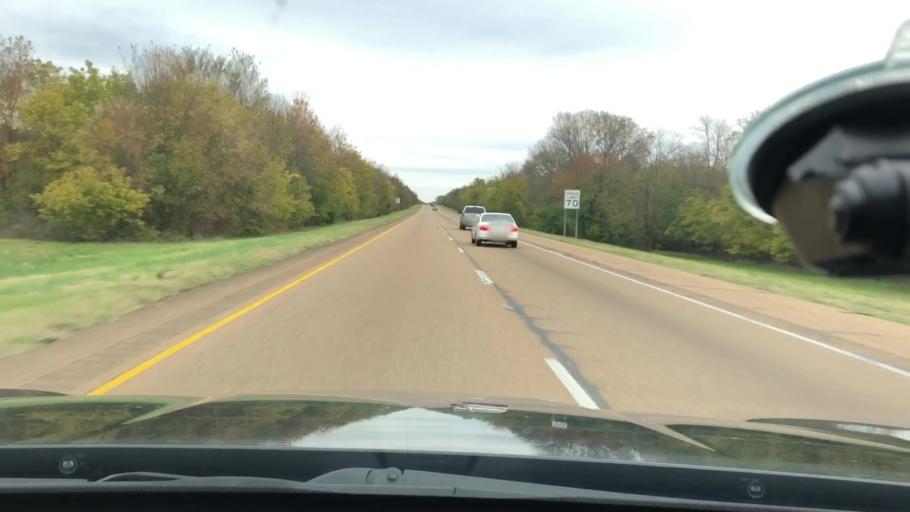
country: US
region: Arkansas
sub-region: Hempstead County
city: Hope
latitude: 33.7434
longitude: -93.5151
